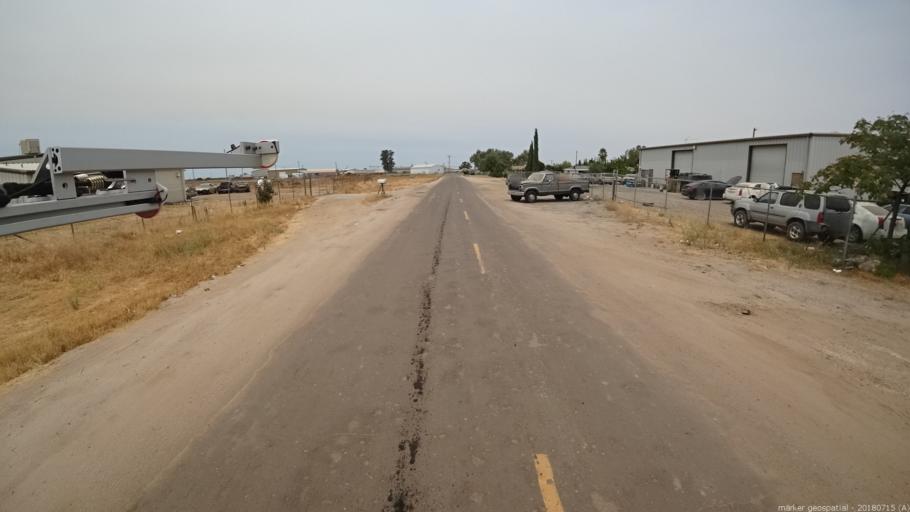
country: US
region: California
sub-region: Madera County
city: Madera Acres
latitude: 37.0037
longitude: -120.1065
